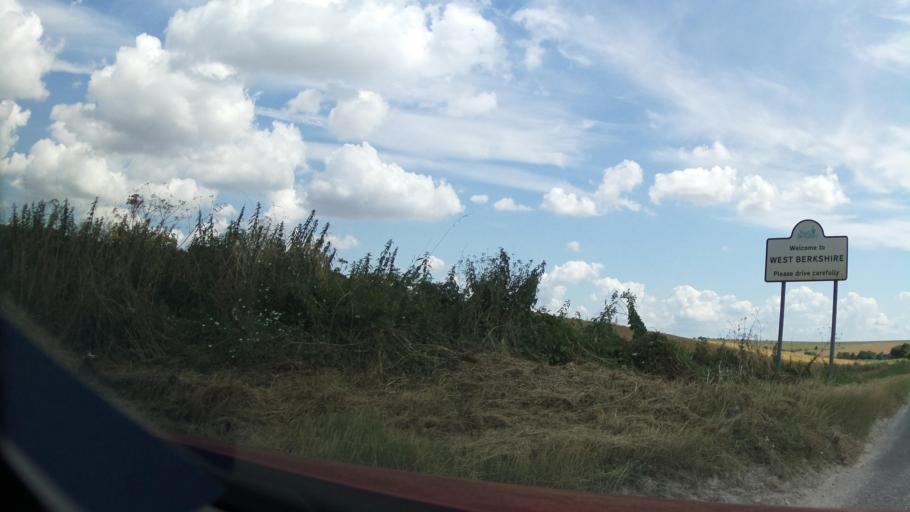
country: GB
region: England
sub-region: West Berkshire
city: Lambourn
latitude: 51.5274
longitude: -1.5842
